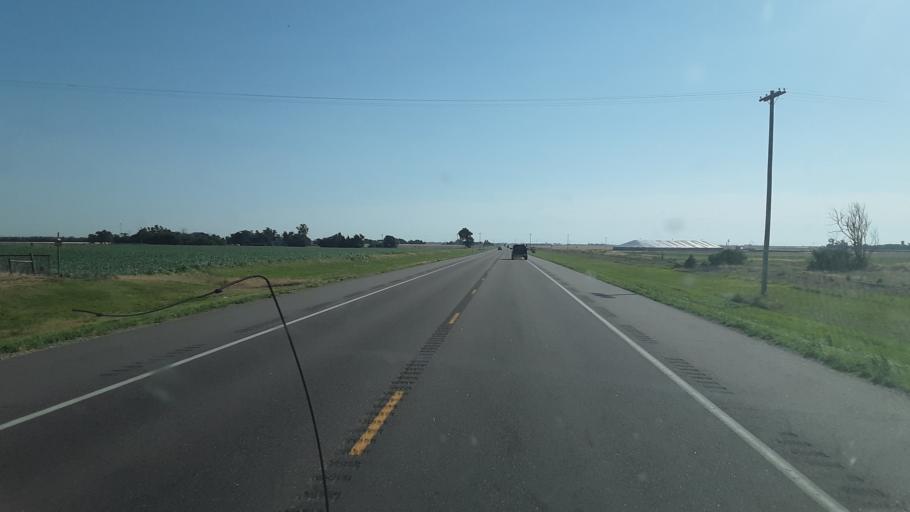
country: US
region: Kansas
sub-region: Pawnee County
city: Larned
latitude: 38.1999
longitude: -99.0702
